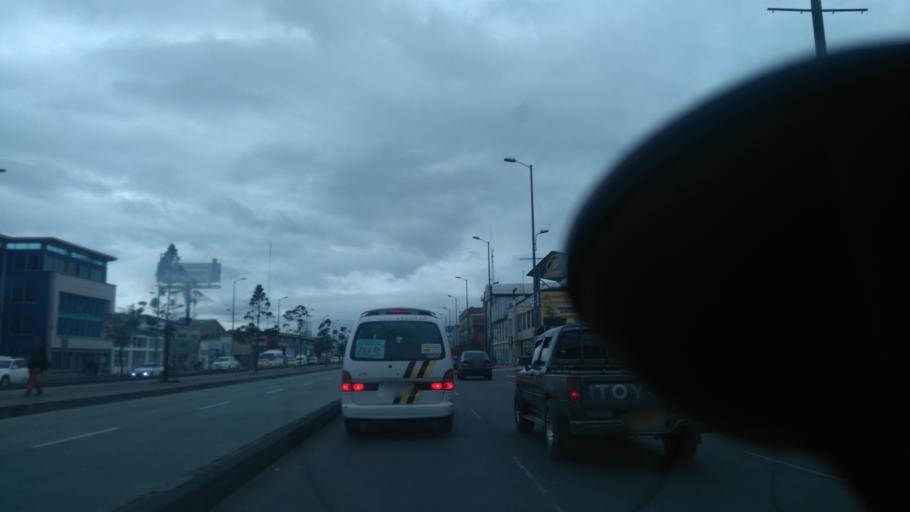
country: CO
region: Bogota D.C.
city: Bogota
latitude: 4.6238
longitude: -74.1024
